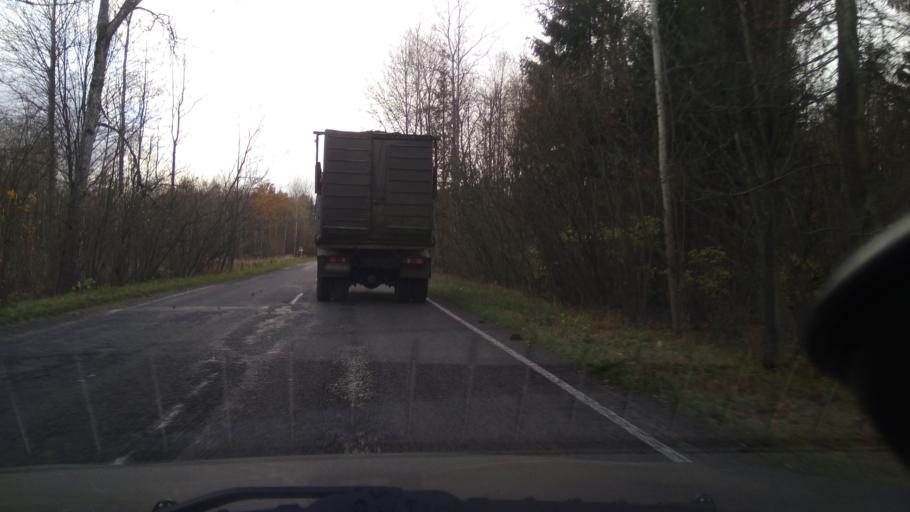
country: BY
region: Minsk
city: Slutsk
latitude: 53.2068
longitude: 27.7753
